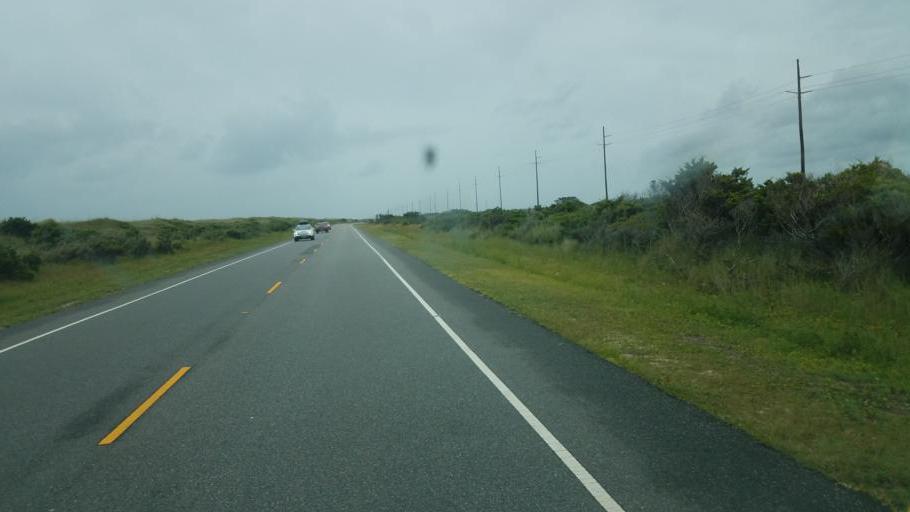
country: US
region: North Carolina
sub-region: Dare County
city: Buxton
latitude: 35.3038
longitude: -75.5125
